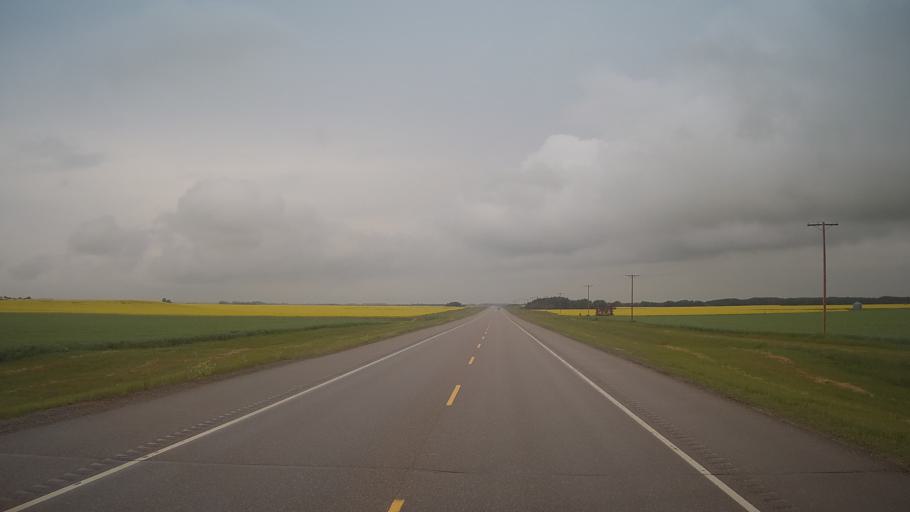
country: CA
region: Saskatchewan
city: Wilkie
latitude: 52.4235
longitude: -108.9027
